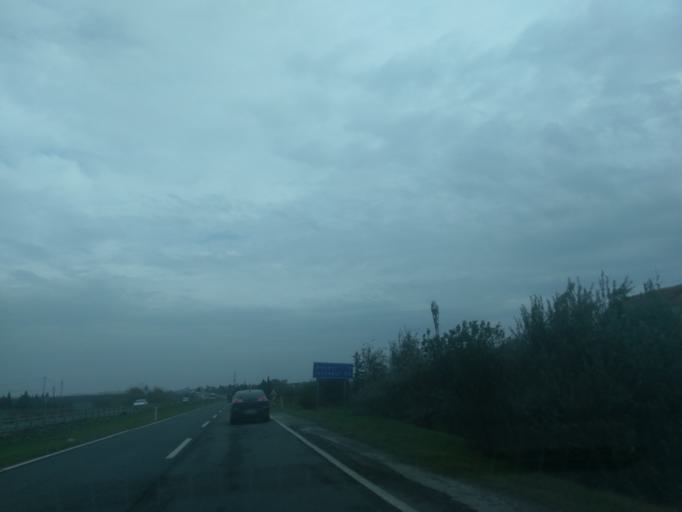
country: TR
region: Istanbul
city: Silivri
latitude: 41.0764
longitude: 28.1671
